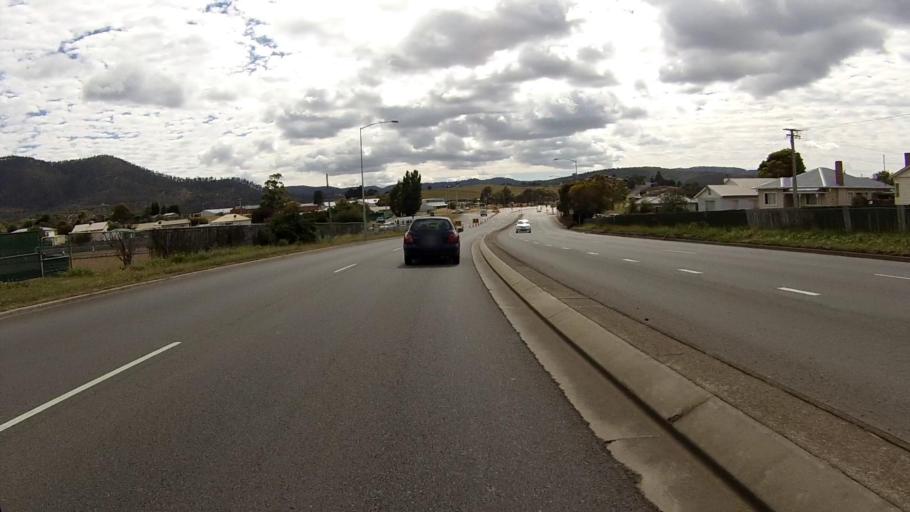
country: AU
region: Tasmania
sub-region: Glenorchy
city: Goodwood
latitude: -42.8239
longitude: 147.2925
